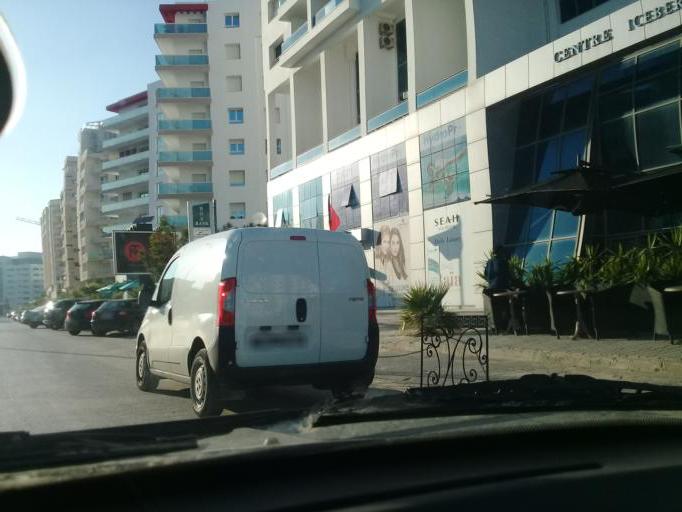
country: TN
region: Tunis
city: La Goulette
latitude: 36.8468
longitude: 10.2787
